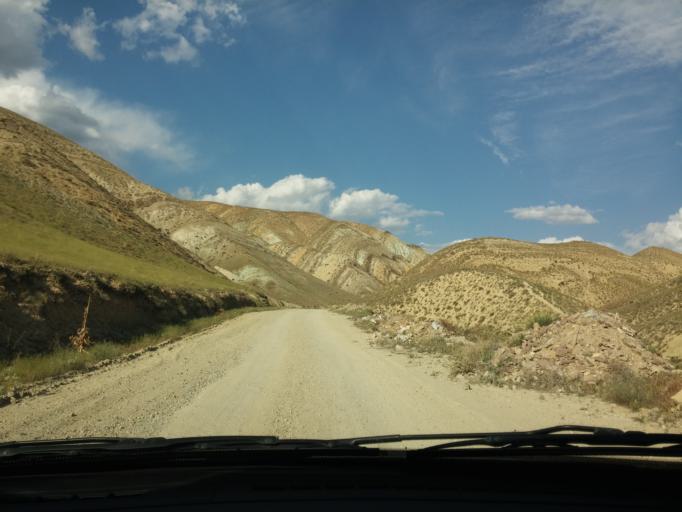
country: IR
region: Tehran
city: Damavand
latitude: 35.5380
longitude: 52.1806
